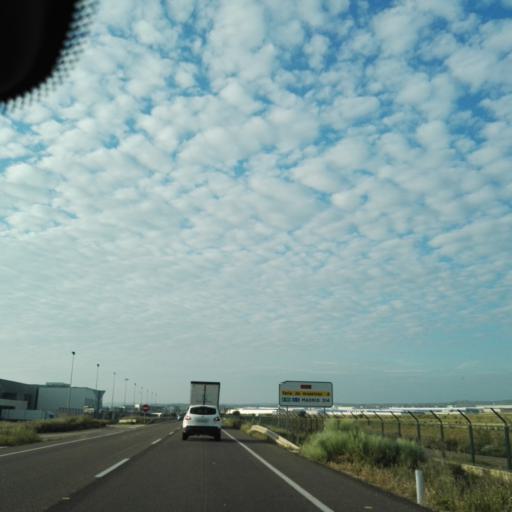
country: ES
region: Aragon
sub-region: Provincia de Zaragoza
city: Utebo
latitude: 41.6581
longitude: -1.0024
